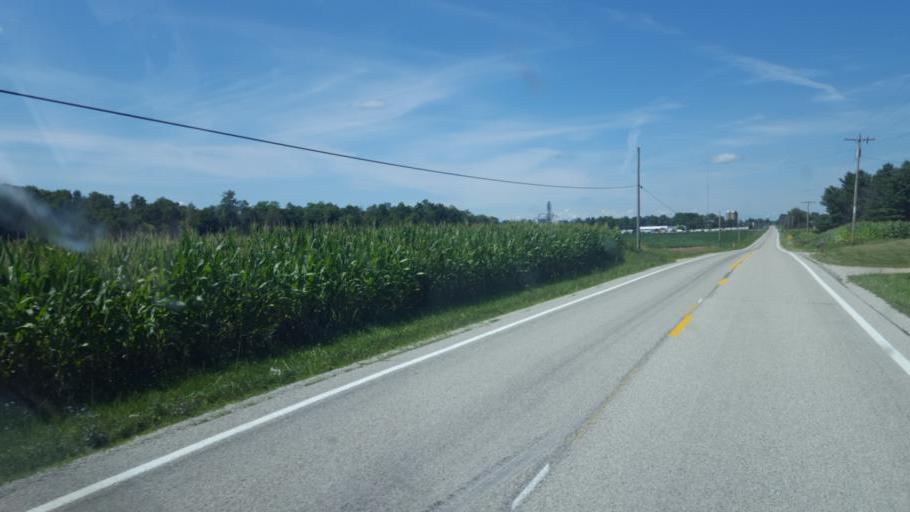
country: US
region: Ohio
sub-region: Knox County
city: Centerburg
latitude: 40.4003
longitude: -82.7638
